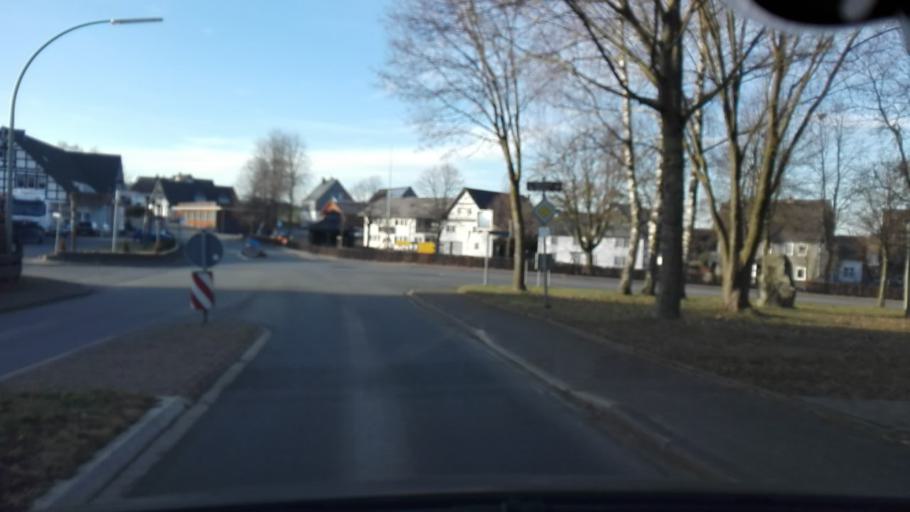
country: DE
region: North Rhine-Westphalia
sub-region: Regierungsbezirk Arnsberg
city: Schmallenberg
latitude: 51.1644
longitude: 8.2293
